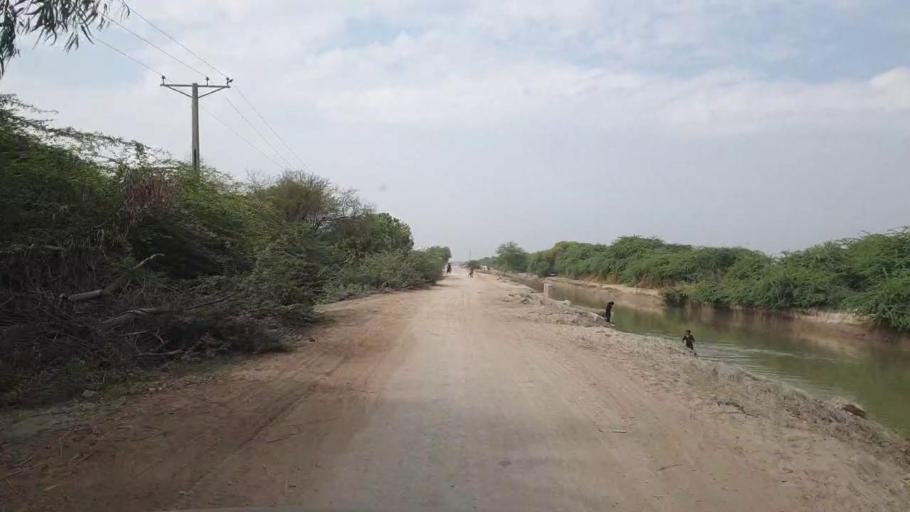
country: PK
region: Sindh
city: Kario
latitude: 24.6311
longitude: 68.5713
